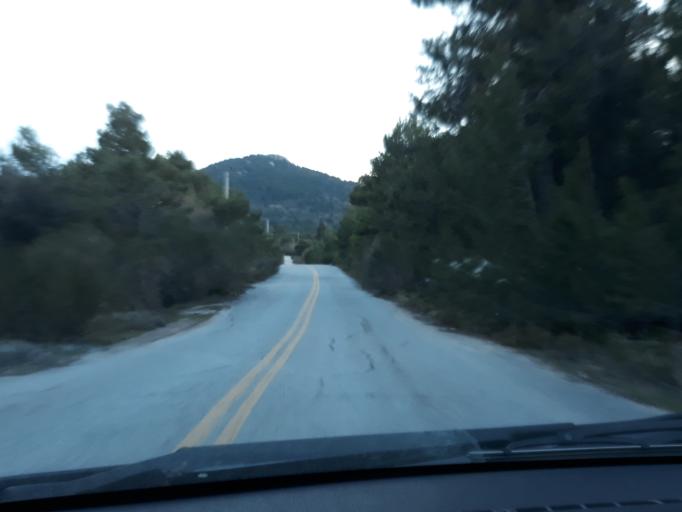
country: GR
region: Attica
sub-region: Nomarchia Anatolikis Attikis
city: Afidnes
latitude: 38.1959
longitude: 23.7935
